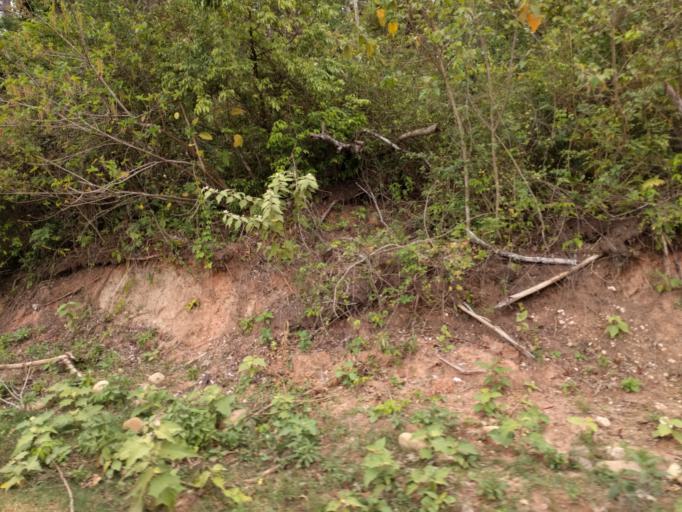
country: BO
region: Santa Cruz
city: Santiago del Torno
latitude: -17.9104
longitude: -63.4374
